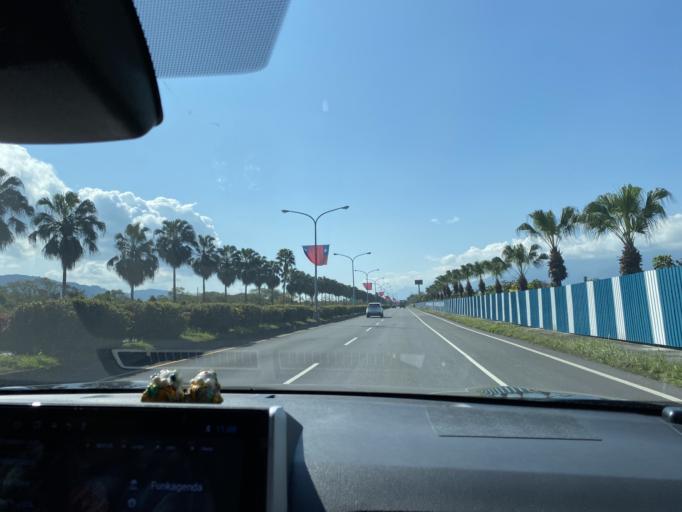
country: TW
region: Taiwan
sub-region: Hualien
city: Hualian
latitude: 23.8683
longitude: 121.5337
